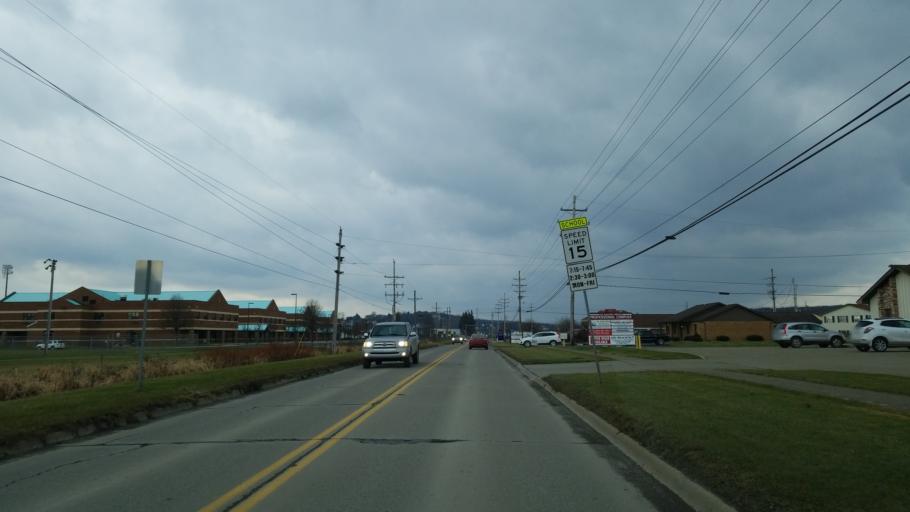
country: US
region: Pennsylvania
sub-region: Clearfield County
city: DuBois
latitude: 41.1235
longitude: -78.7524
